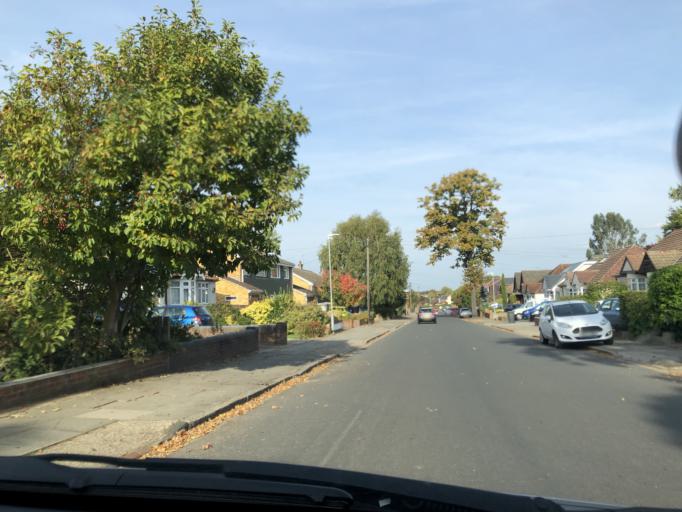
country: GB
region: England
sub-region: Greater London
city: Bexley
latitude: 51.4279
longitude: 0.1678
